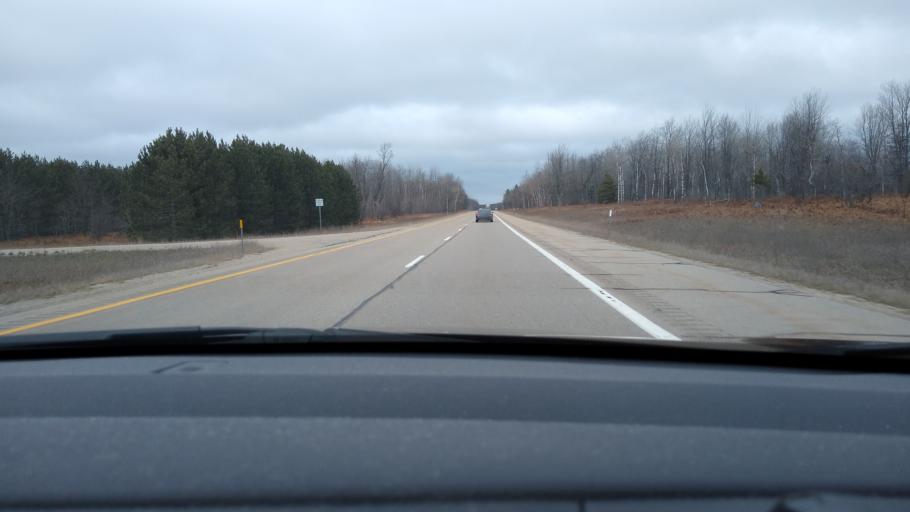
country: US
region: Michigan
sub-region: Crawford County
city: Grayling
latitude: 44.7976
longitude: -84.7134
